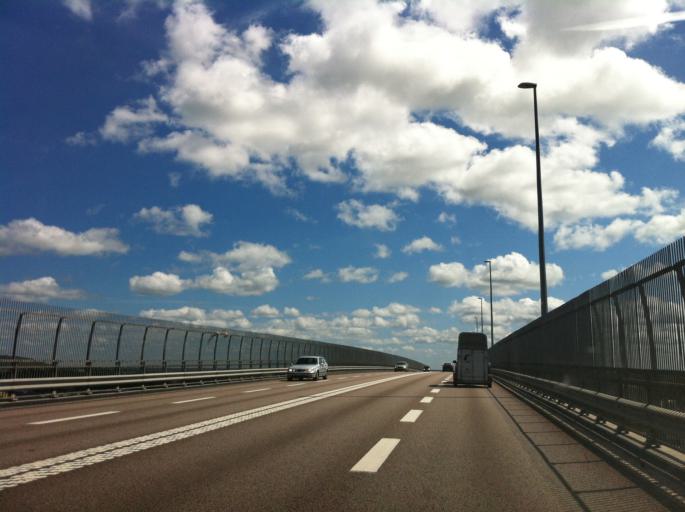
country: SE
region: Vaestra Goetaland
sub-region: Trollhattan
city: Trollhattan
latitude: 58.3199
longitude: 12.3030
